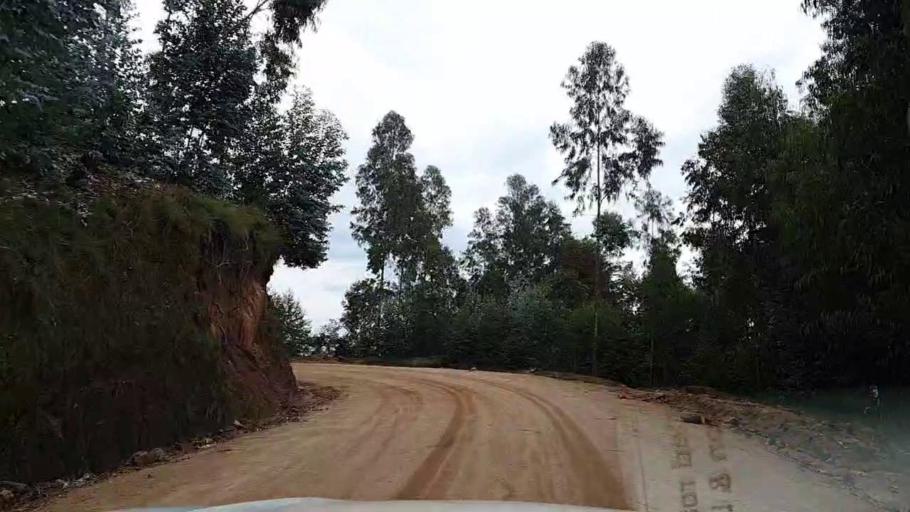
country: RW
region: Southern Province
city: Nzega
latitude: -2.3786
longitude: 29.4487
